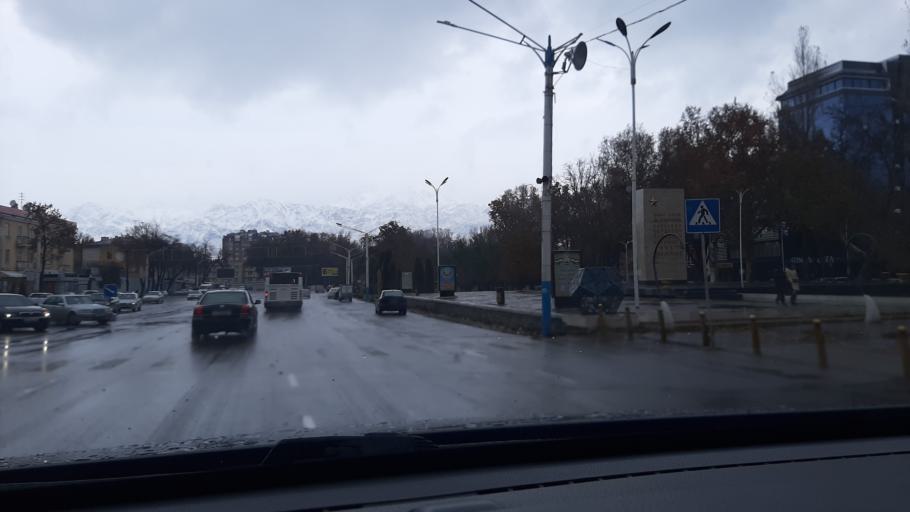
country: TJ
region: Viloyati Sughd
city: Khujand
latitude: 40.2835
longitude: 69.6236
